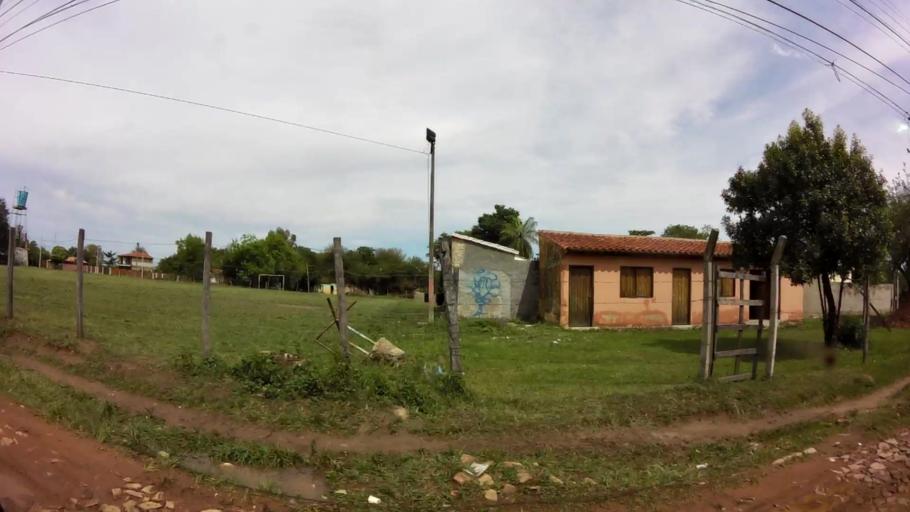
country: PY
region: Central
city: Limpio
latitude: -25.1865
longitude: -57.4775
